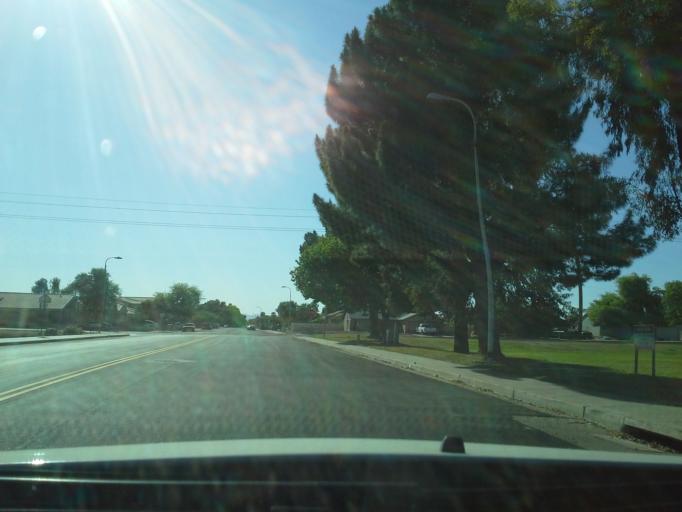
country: US
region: Arizona
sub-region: Maricopa County
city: Glendale
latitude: 33.5310
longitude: -112.2108
